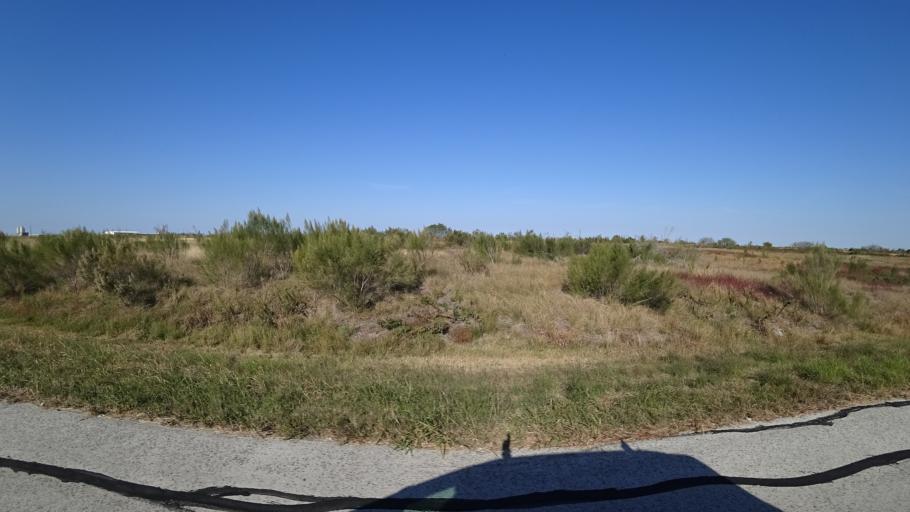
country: US
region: Texas
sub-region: Travis County
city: Onion Creek
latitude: 30.0854
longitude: -97.6874
